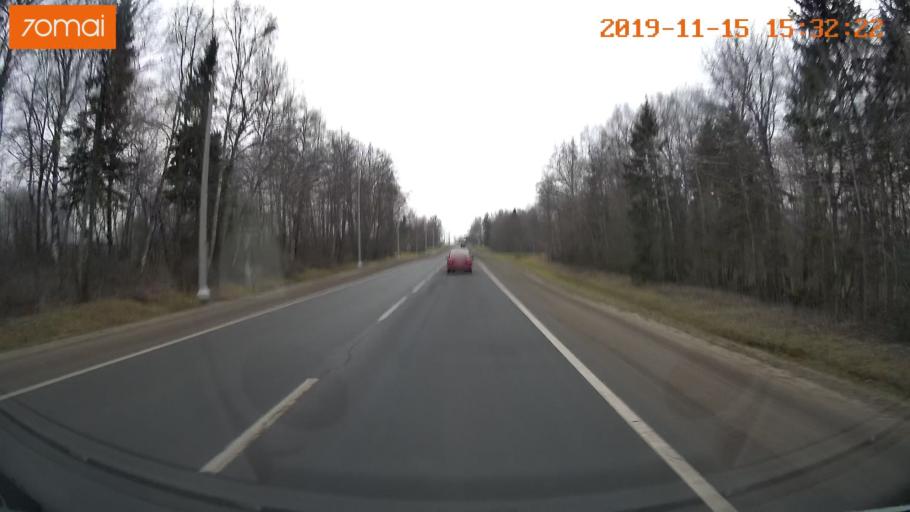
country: RU
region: Jaroslavl
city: Danilov
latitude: 58.0910
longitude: 40.1010
